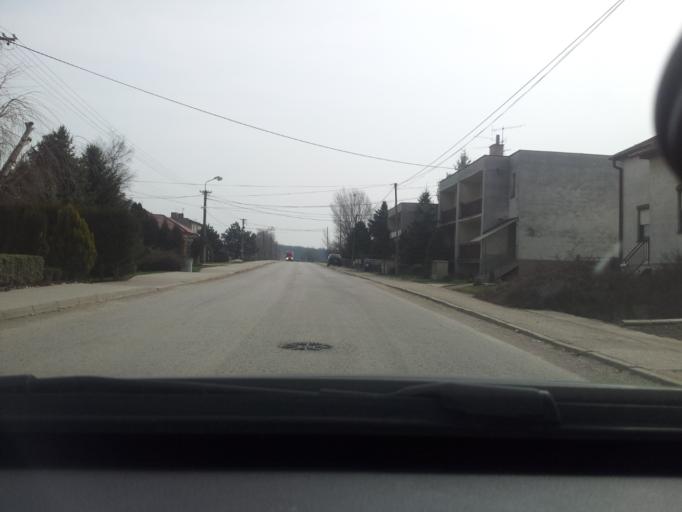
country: SK
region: Trnavsky
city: Leopoldov
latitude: 48.4574
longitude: 17.7207
